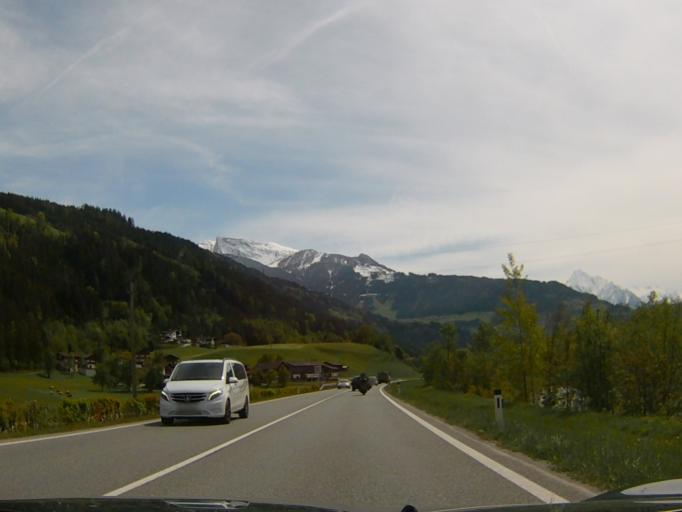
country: AT
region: Tyrol
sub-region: Politischer Bezirk Schwaz
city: Rohrberg
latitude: 47.2547
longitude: 11.9023
